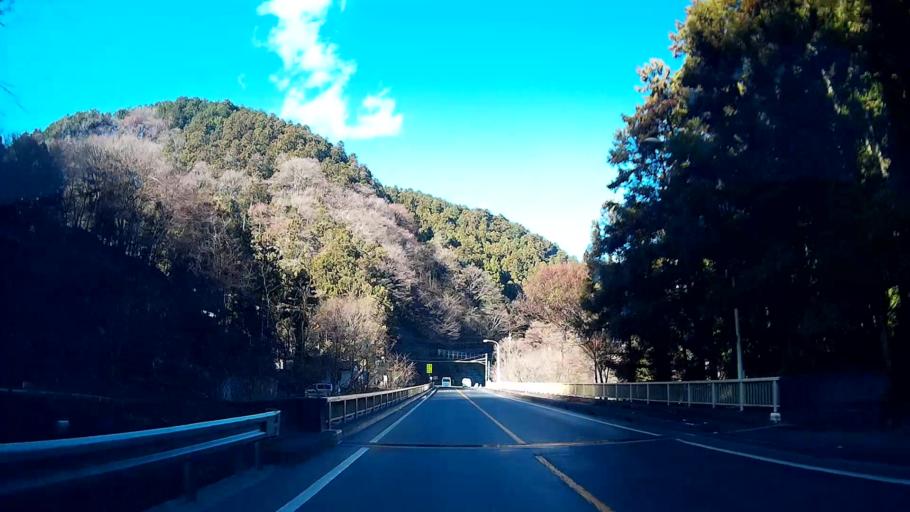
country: JP
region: Saitama
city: Chichibu
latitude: 35.9735
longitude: 139.1177
